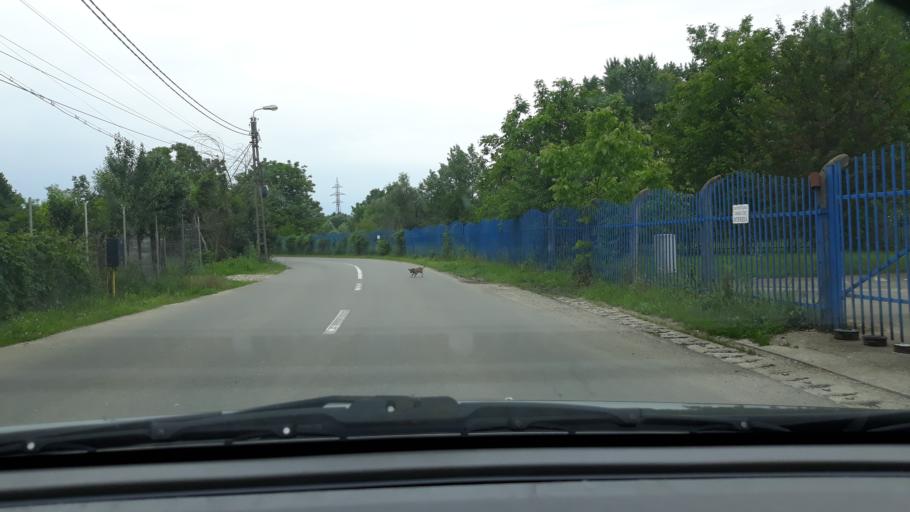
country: RO
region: Bihor
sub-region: Comuna Sanmartin
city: Sanmartin
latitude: 47.0507
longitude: 21.9819
